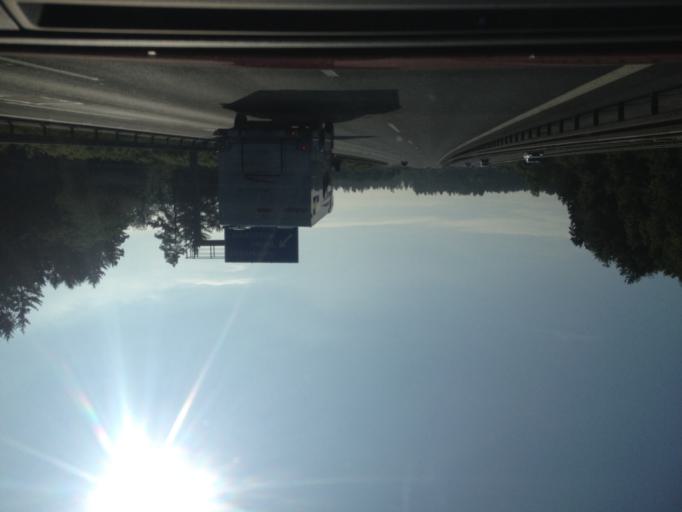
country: DE
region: Bavaria
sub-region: Regierungsbezirk Mittelfranken
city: Kirchensittenbach
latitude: 49.6188
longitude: 11.4028
